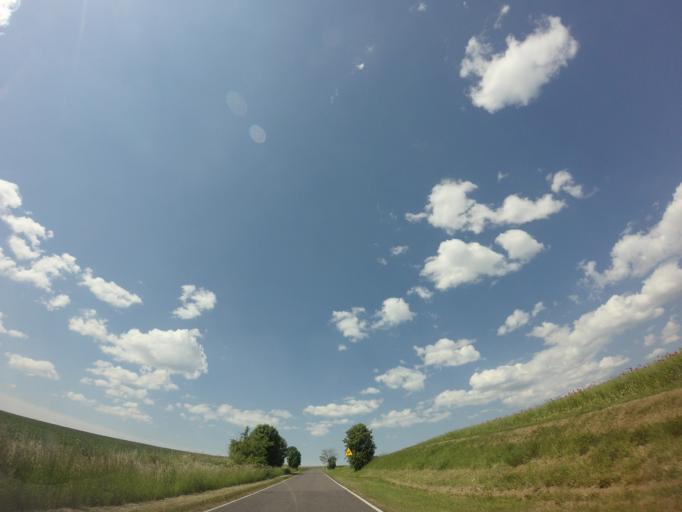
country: PL
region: West Pomeranian Voivodeship
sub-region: Powiat choszczenski
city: Pelczyce
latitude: 53.1052
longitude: 15.2587
